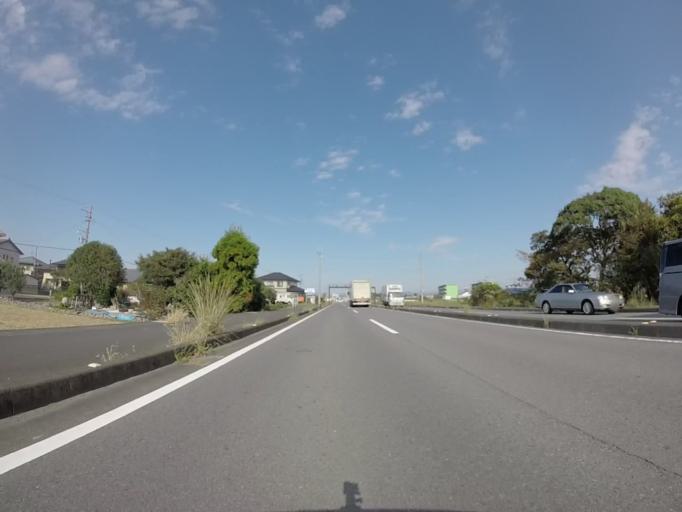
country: JP
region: Shizuoka
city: Shimada
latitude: 34.7878
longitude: 138.2432
